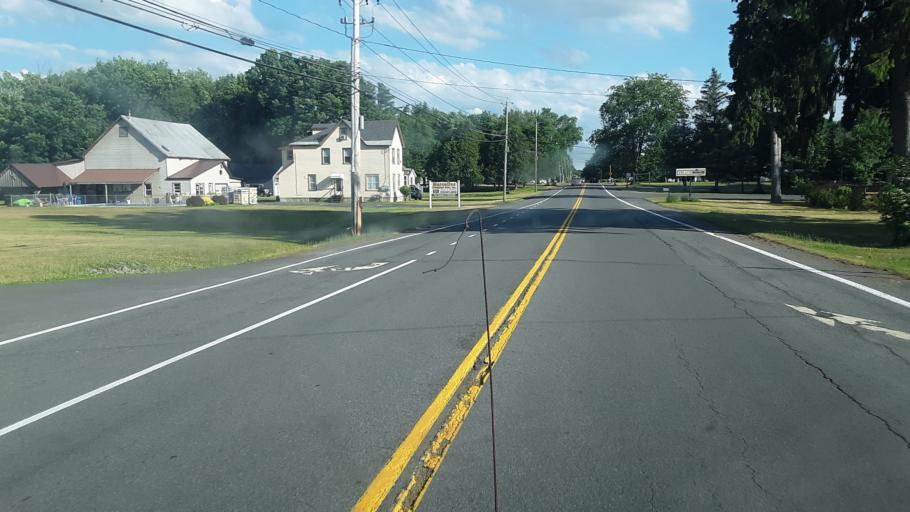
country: US
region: New York
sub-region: Oneida County
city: Rome
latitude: 43.2579
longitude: -75.4616
